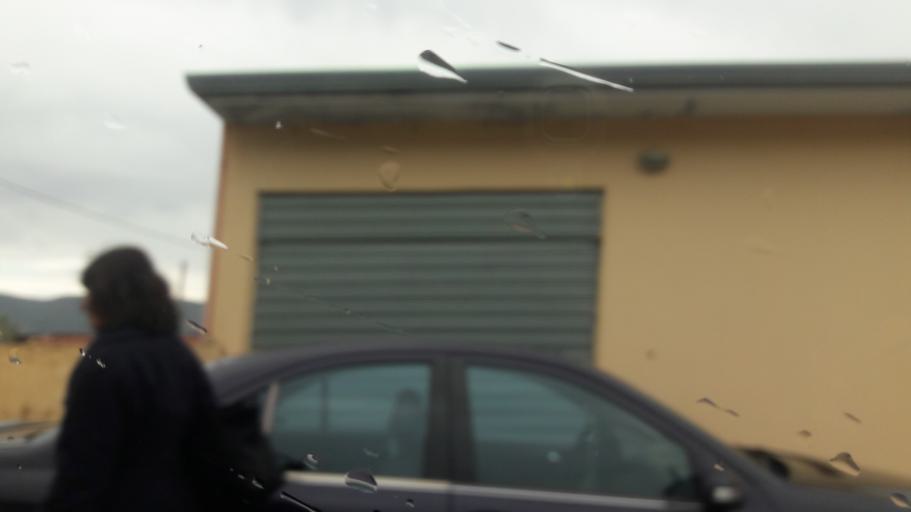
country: AL
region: Shkoder
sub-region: Rrethi i Shkodres
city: Berdica e Madhe
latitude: 41.9527
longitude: 19.5179
